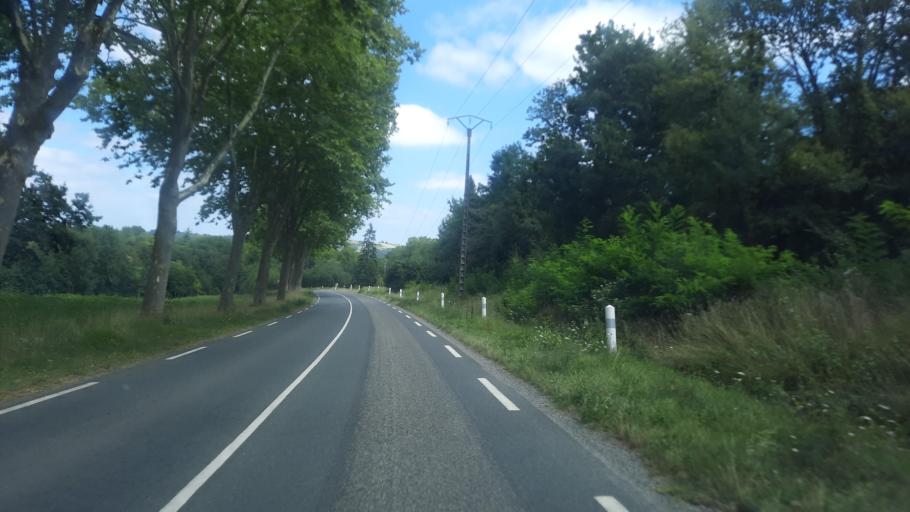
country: FR
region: Midi-Pyrenees
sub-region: Departement de la Haute-Garonne
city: Boulogne-sur-Gesse
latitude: 43.2928
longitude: 0.6608
